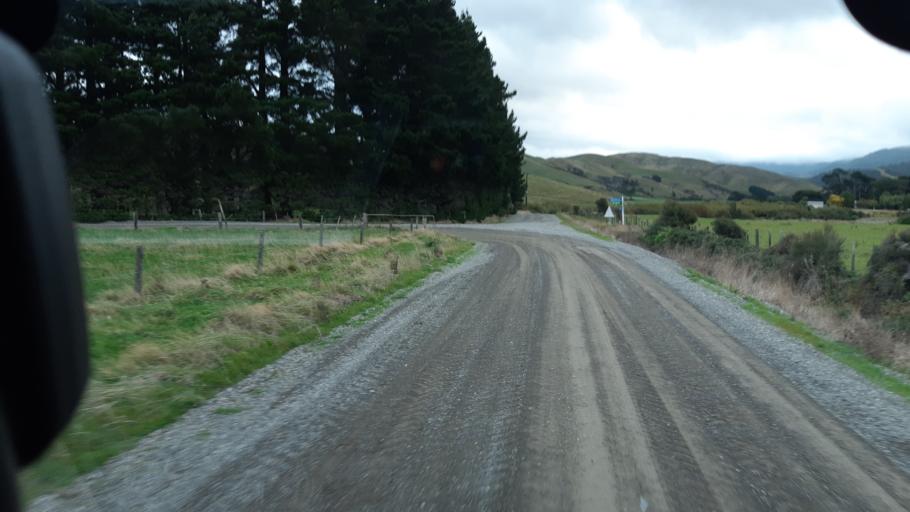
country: NZ
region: Manawatu-Wanganui
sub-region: Palmerston North City
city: Palmerston North
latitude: -40.6145
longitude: 175.6098
